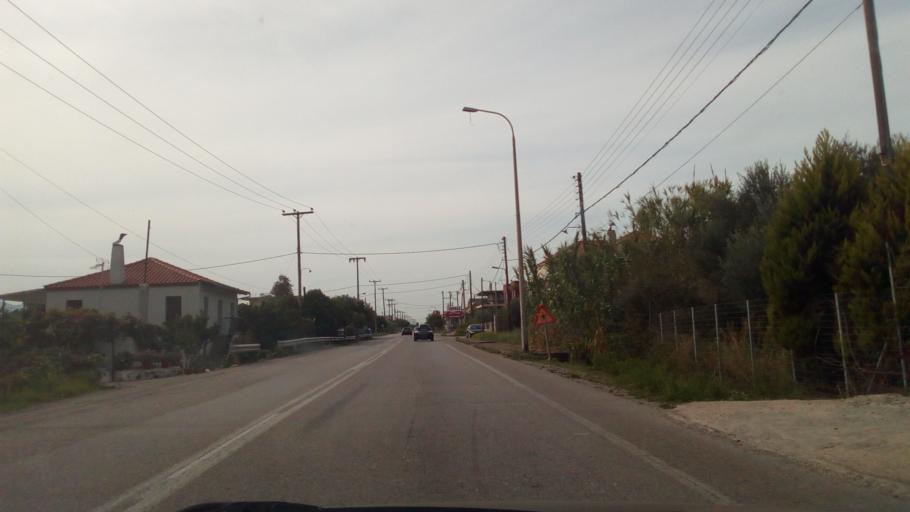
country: GR
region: West Greece
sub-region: Nomos Aitolias kai Akarnanias
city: Antirrio
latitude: 38.3643
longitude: 21.7782
